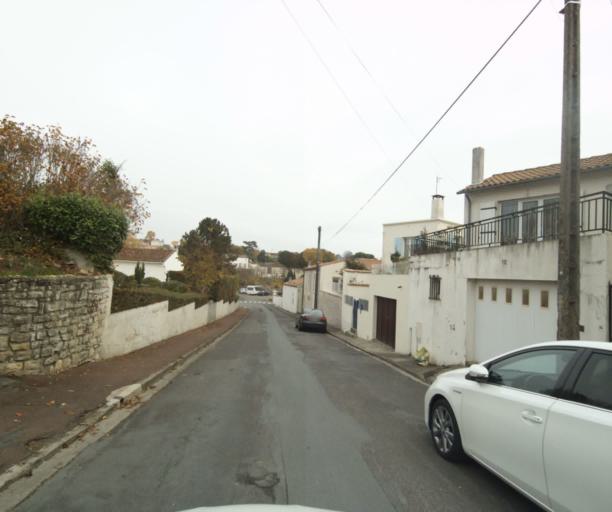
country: FR
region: Poitou-Charentes
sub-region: Departement de la Charente-Maritime
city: Saintes
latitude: 45.7450
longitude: -0.6457
